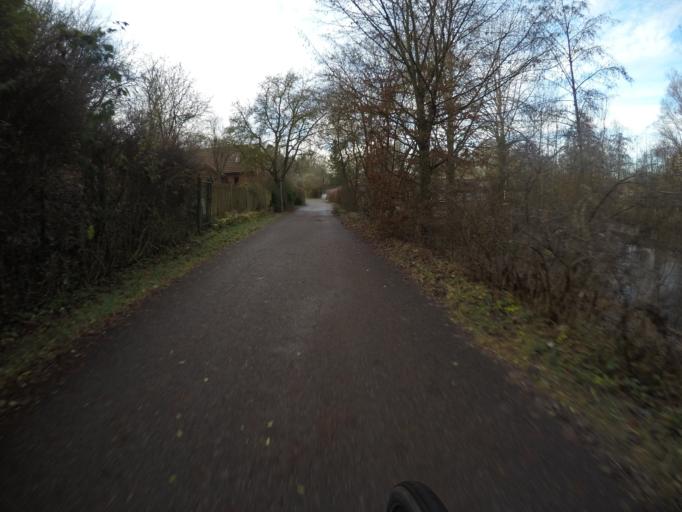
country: DE
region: Baden-Wuerttemberg
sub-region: Regierungsbezirk Stuttgart
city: Sindelfingen
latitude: 48.7151
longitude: 9.0080
